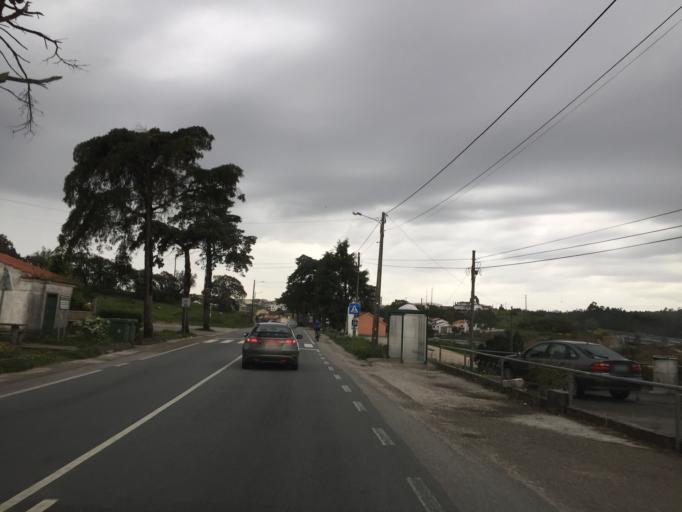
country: PT
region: Leiria
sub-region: Leiria
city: Santa Catarina da Serra
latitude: 39.6714
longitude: -8.6837
